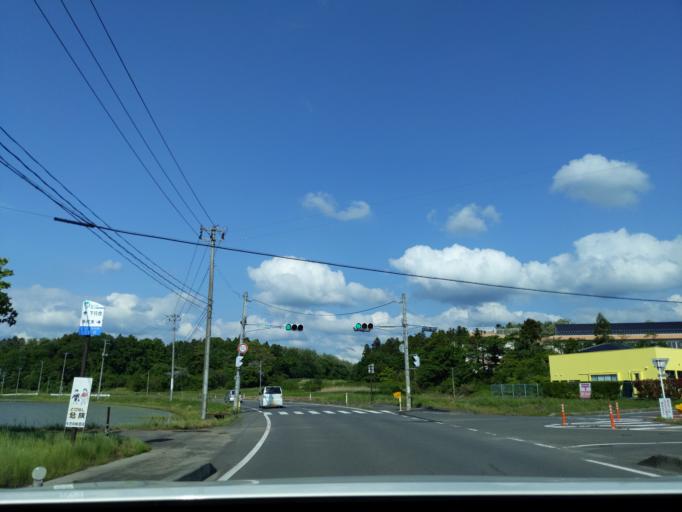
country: JP
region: Fukushima
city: Koriyama
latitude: 37.3664
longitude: 140.4064
